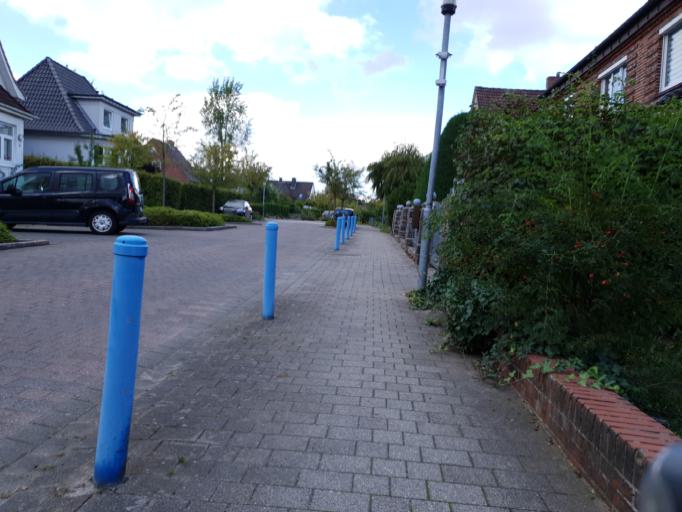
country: DE
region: Schleswig-Holstein
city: Kronshagen
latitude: 54.3295
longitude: 10.0946
